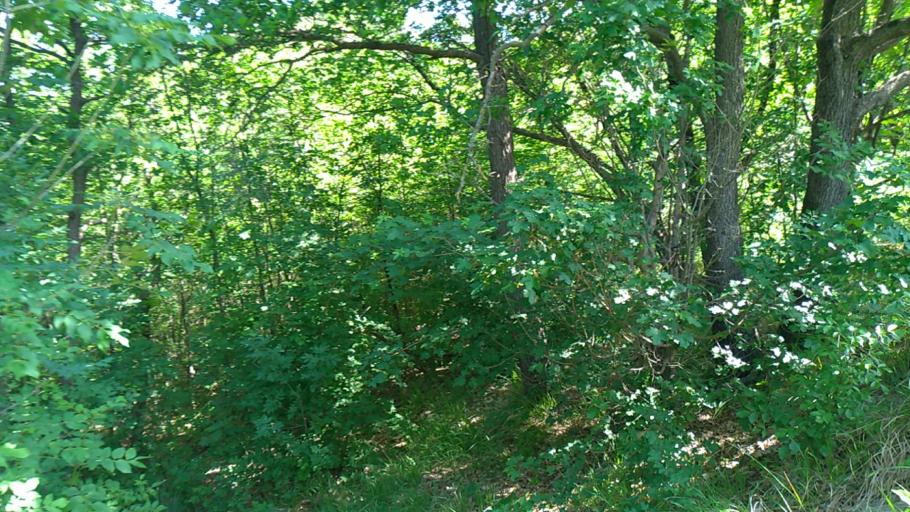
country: IT
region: Emilia-Romagna
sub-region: Provincia di Modena
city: Guiglia
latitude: 44.4114
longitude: 10.9284
